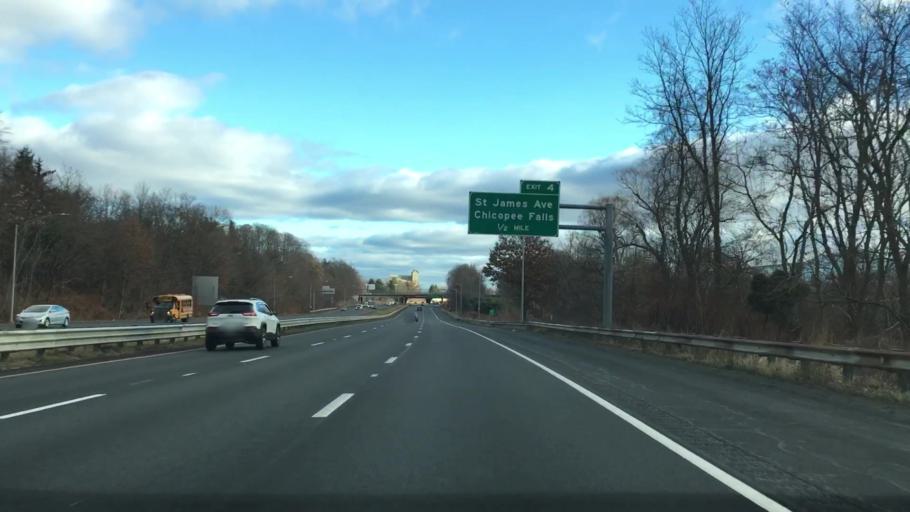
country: US
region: Massachusetts
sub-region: Hampden County
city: Springfield
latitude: 42.1225
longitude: -72.5737
